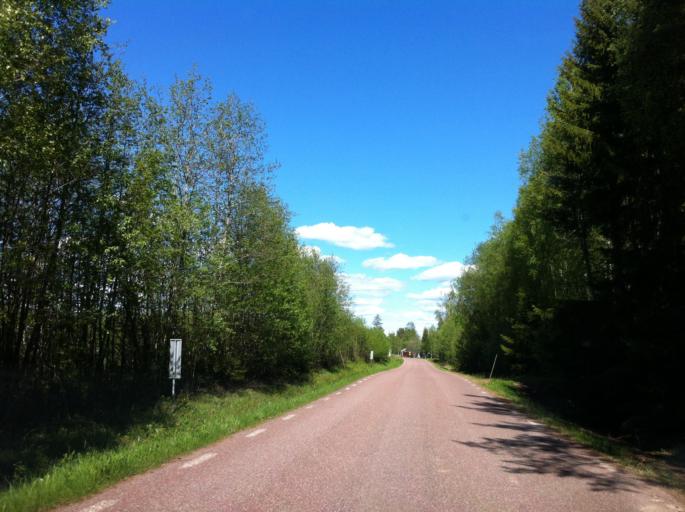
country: SE
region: Dalarna
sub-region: Mora Kommun
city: Mora
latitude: 60.9611
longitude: 14.6786
